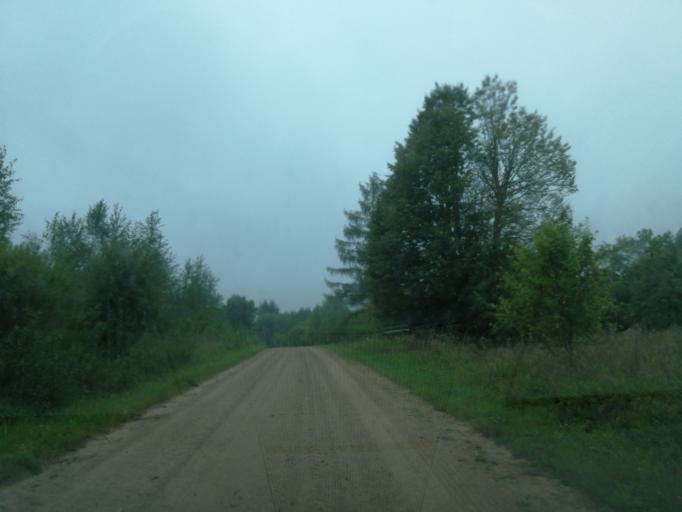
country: LV
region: Preilu Rajons
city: Jaunaglona
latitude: 56.3173
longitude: 27.0090
